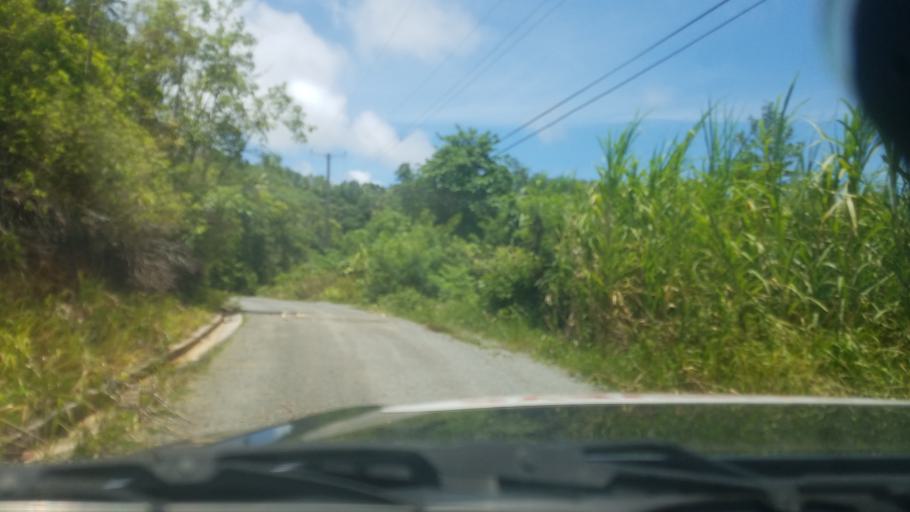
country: LC
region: Praslin
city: Praslin
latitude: 13.8690
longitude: -60.9145
